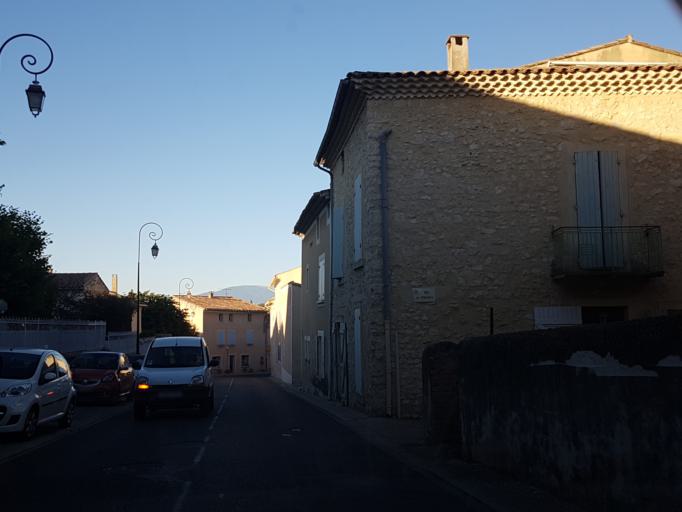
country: FR
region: Provence-Alpes-Cote d'Azur
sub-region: Departement du Vaucluse
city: Velleron
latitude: 43.9569
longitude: 5.0307
